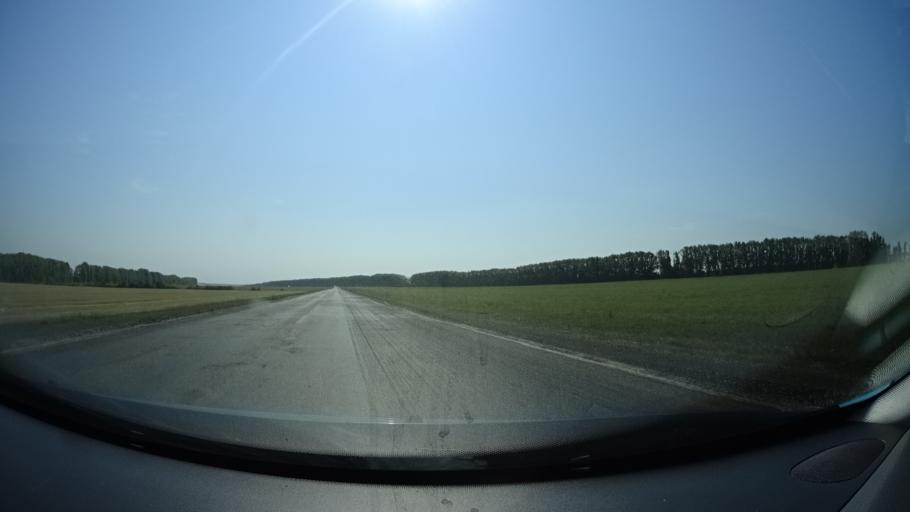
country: RU
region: Bashkortostan
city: Kabakovo
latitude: 54.4589
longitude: 55.9666
